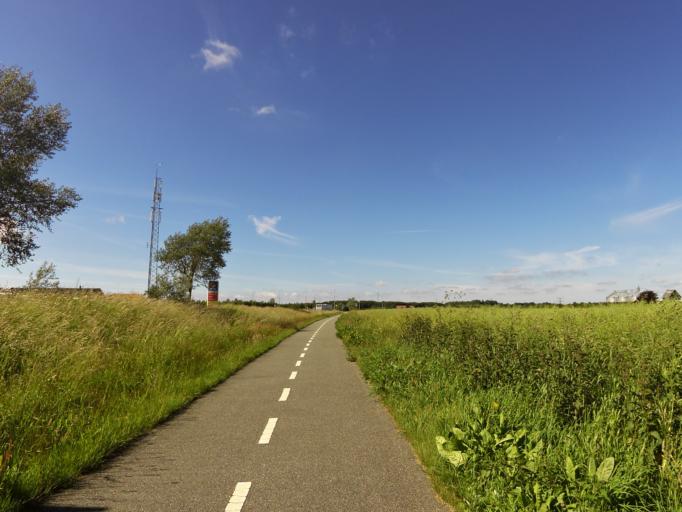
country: DK
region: South Denmark
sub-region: Aabenraa Kommune
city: Rodekro
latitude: 55.0748
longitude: 9.2208
